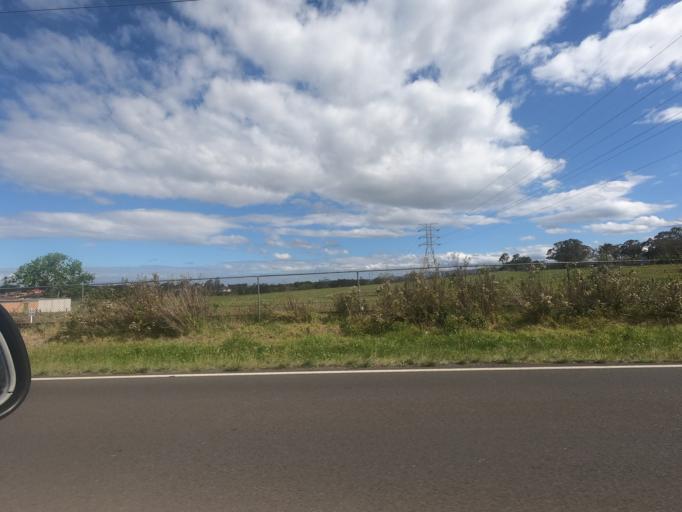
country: AU
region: New South Wales
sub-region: Wollongong
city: Dapto
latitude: -34.4796
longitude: 150.7735
